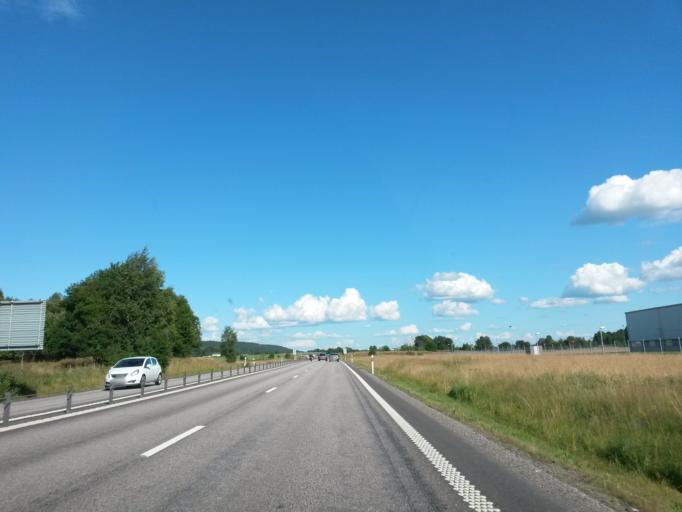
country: SE
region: Vaestra Goetaland
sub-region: Trollhattan
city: Trollhattan
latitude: 58.2969
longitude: 12.3531
